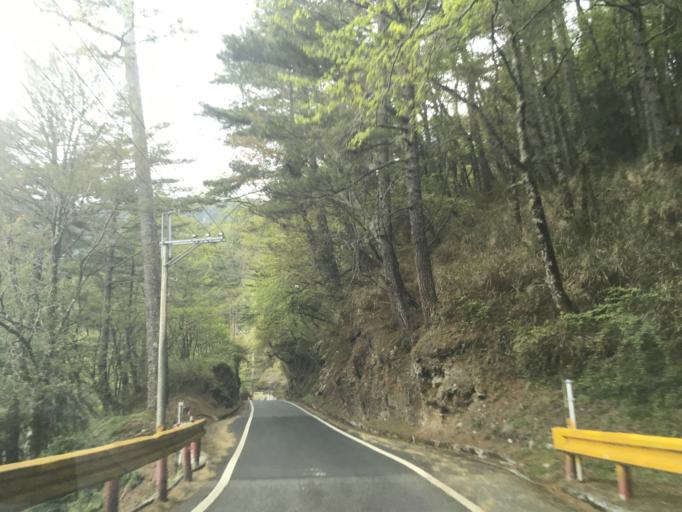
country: TW
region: Taiwan
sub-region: Hualien
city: Hualian
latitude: 24.1873
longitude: 121.3294
